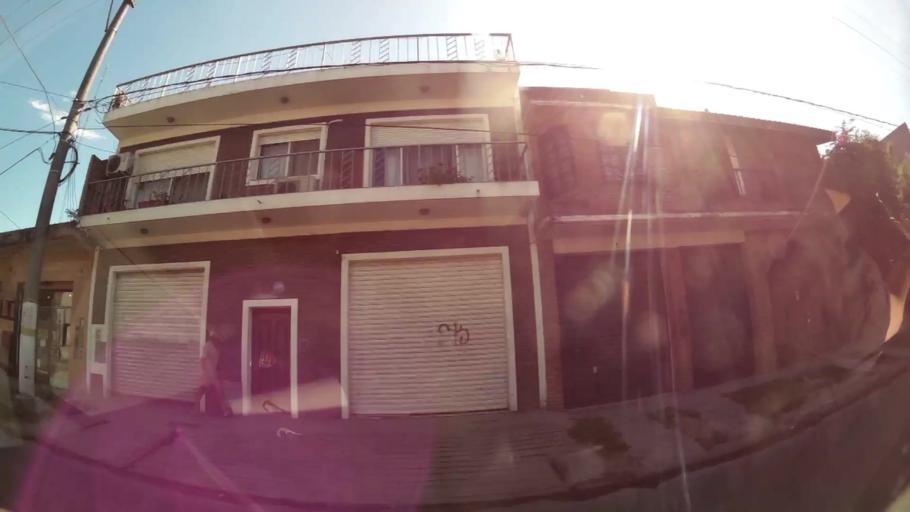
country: AR
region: Buenos Aires
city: Santa Catalina - Dique Lujan
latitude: -34.4849
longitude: -58.6969
